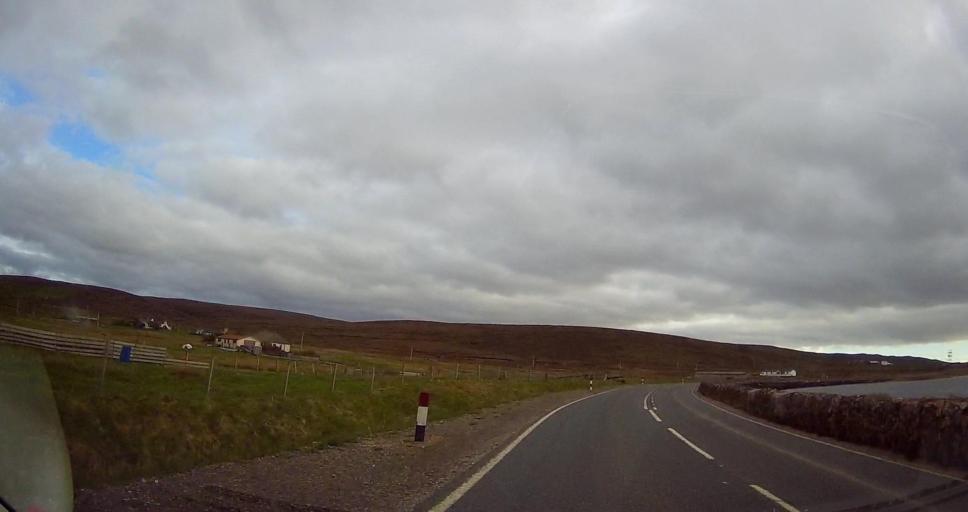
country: GB
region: Scotland
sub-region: Shetland Islands
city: Lerwick
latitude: 60.4447
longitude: -1.2588
